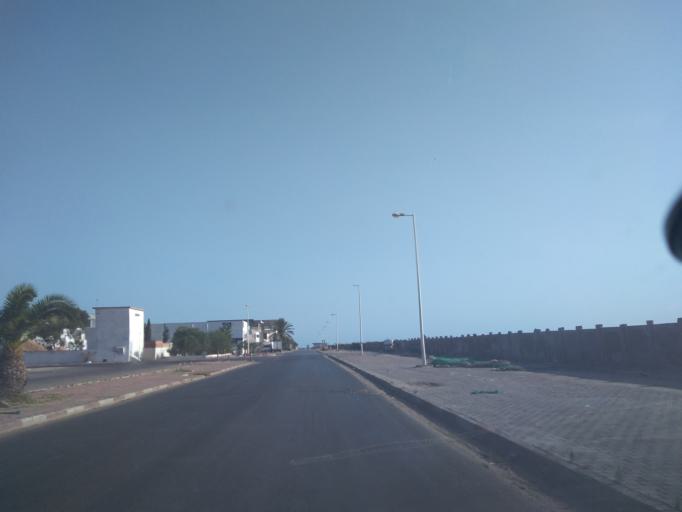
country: TN
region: Safaqis
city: Sfax
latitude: 34.7163
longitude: 10.7608
